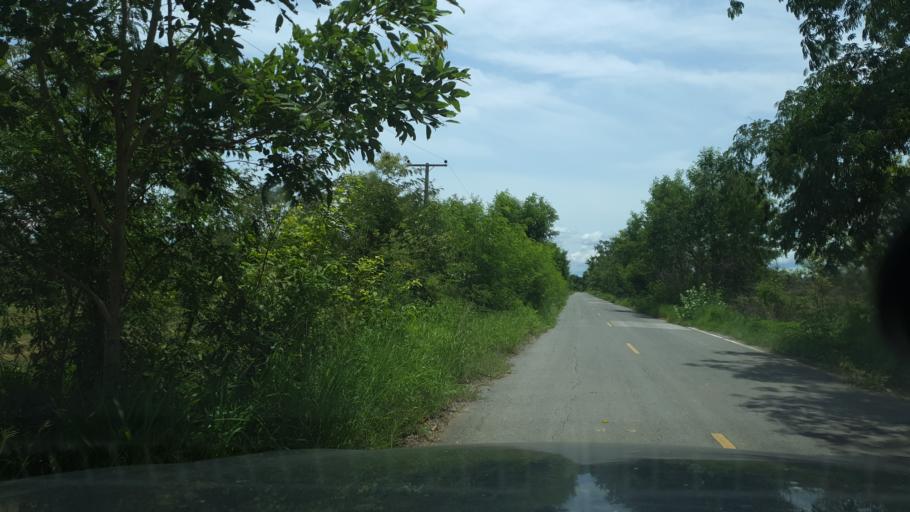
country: TH
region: Sukhothai
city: Ban Na
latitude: 17.0943
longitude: 99.6795
